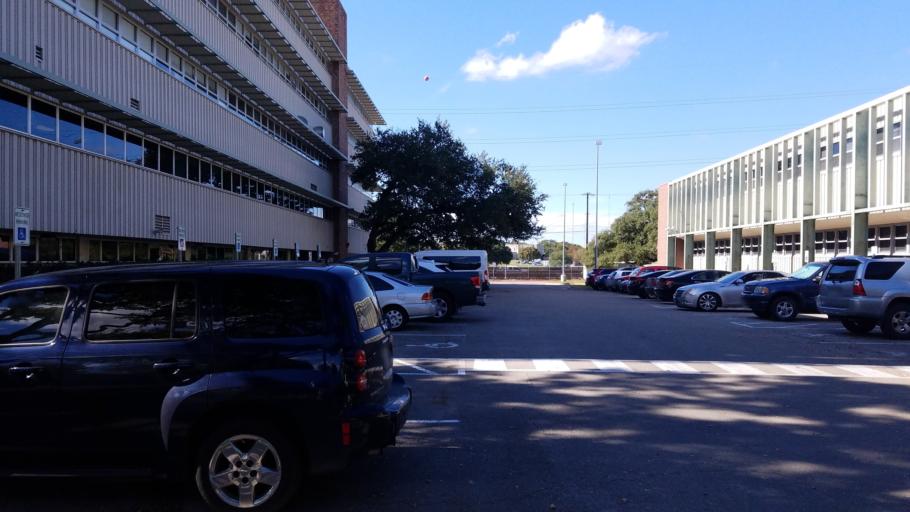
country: US
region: Texas
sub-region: Travis County
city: Austin
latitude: 30.3117
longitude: -97.7557
